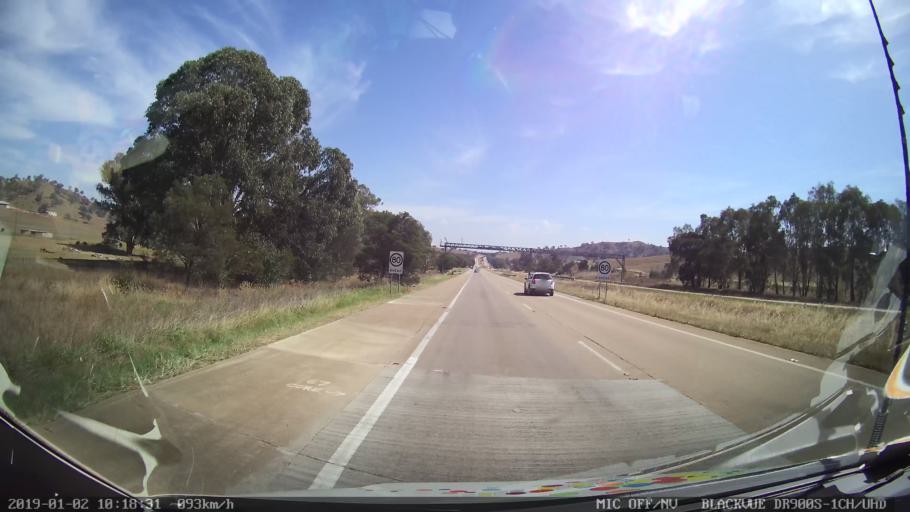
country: AU
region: New South Wales
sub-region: Gundagai
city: Gundagai
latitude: -35.0089
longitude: 148.1109
